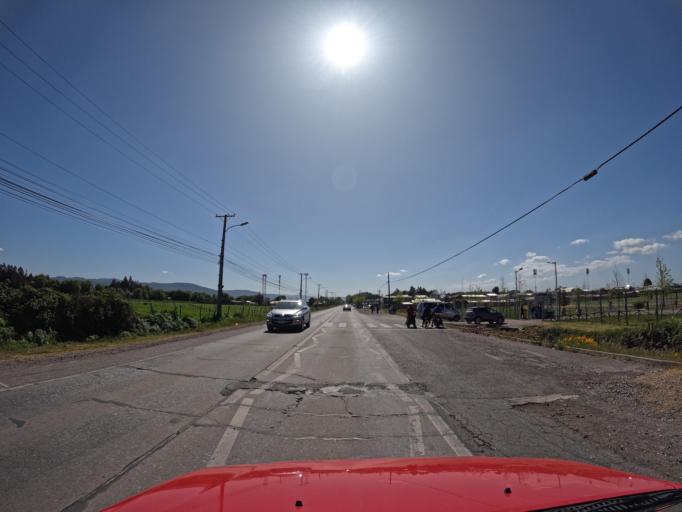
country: CL
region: Maule
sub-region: Provincia de Curico
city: Molina
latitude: -35.0624
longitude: -71.2600
